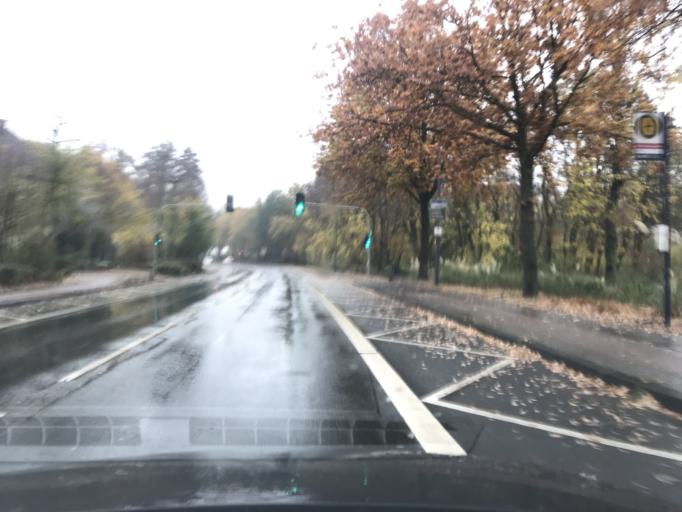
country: DE
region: North Rhine-Westphalia
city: Oelde
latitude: 51.8190
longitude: 8.1427
